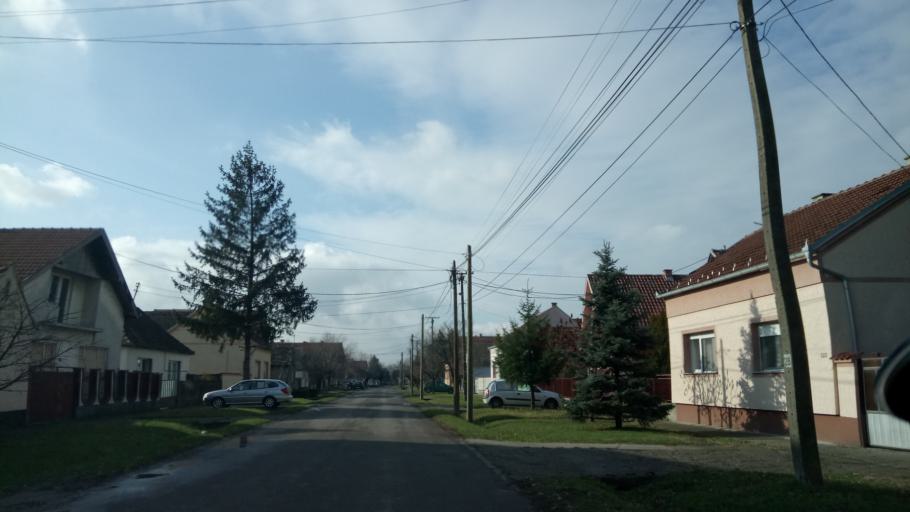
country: RS
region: Autonomna Pokrajina Vojvodina
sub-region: Sremski Okrug
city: Stara Pazova
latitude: 44.9811
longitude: 20.1470
